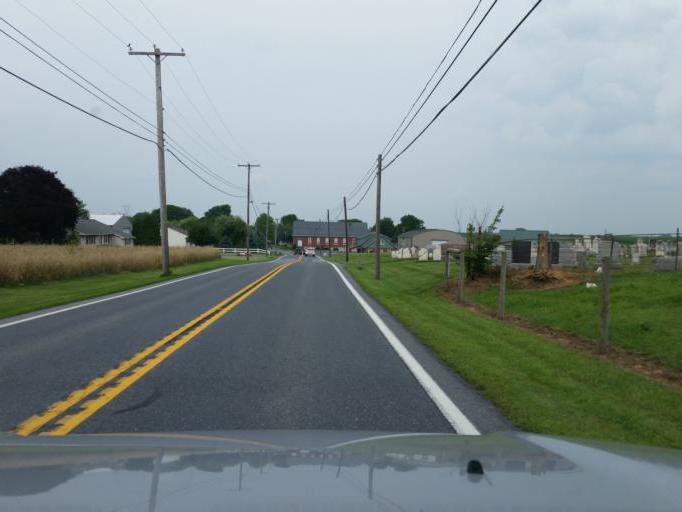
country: US
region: Pennsylvania
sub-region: Lancaster County
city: Salunga
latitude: 40.1291
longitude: -76.4464
